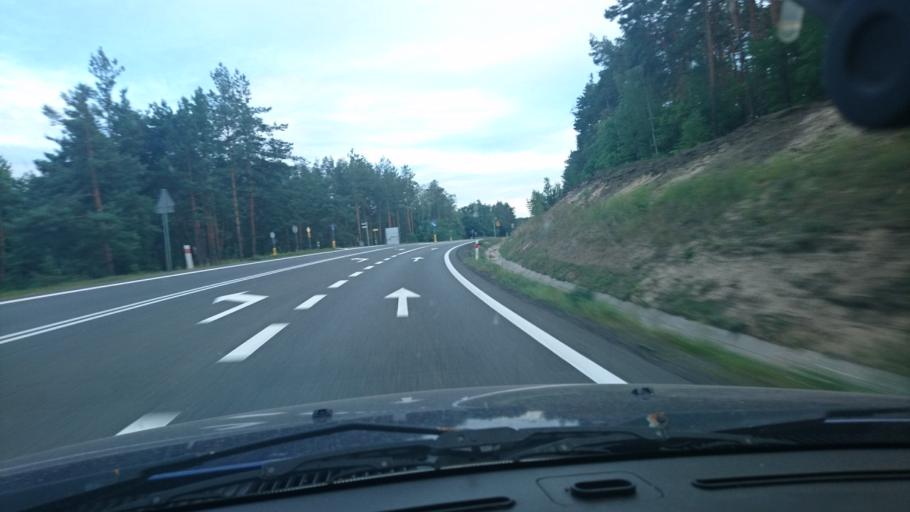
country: PL
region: Silesian Voivodeship
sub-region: Powiat tarnogorski
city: Tworog
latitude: 50.5978
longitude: 18.7027
